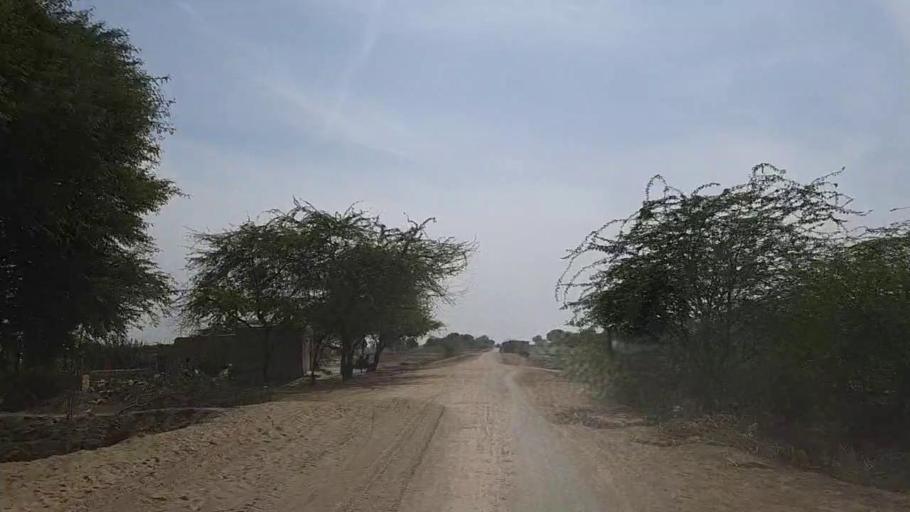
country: PK
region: Sindh
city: Kunri
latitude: 25.1844
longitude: 69.4591
